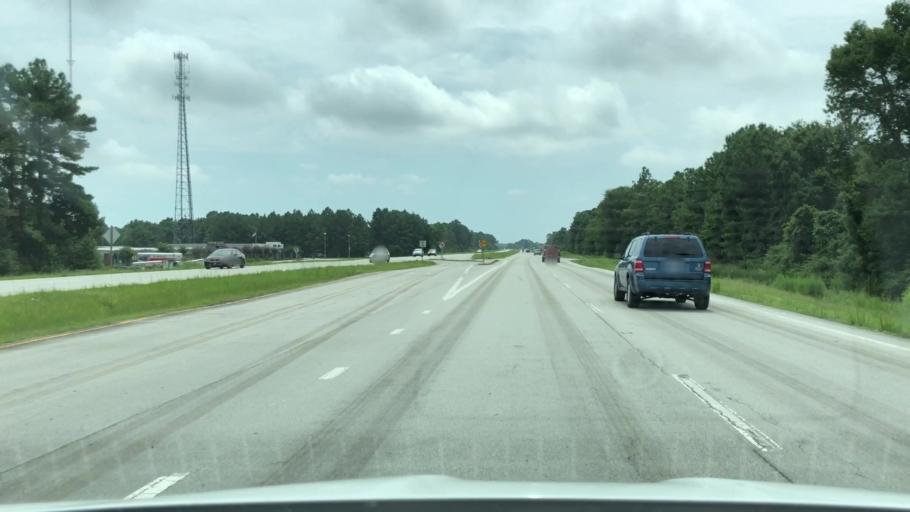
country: US
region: North Carolina
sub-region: Carteret County
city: Newport
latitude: 34.8034
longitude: -76.8787
